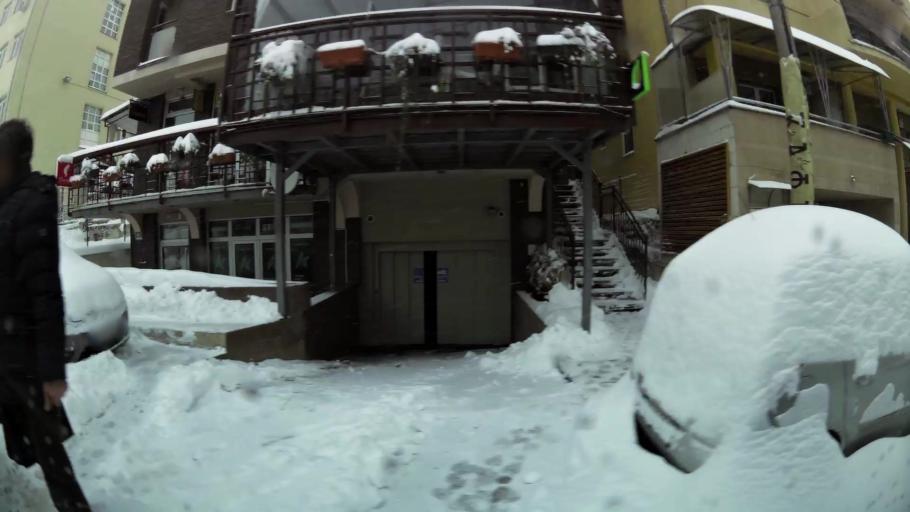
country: RS
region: Central Serbia
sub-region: Belgrade
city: Vracar
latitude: 44.7913
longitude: 20.4780
